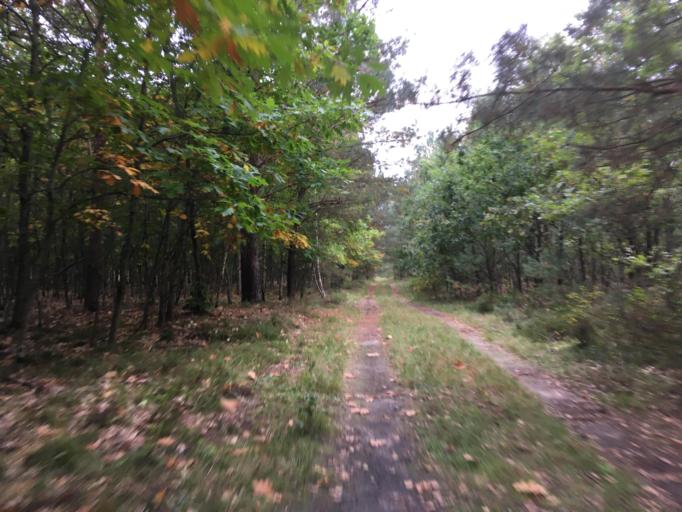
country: DE
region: Brandenburg
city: Birkenwerder
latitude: 52.7039
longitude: 13.3489
